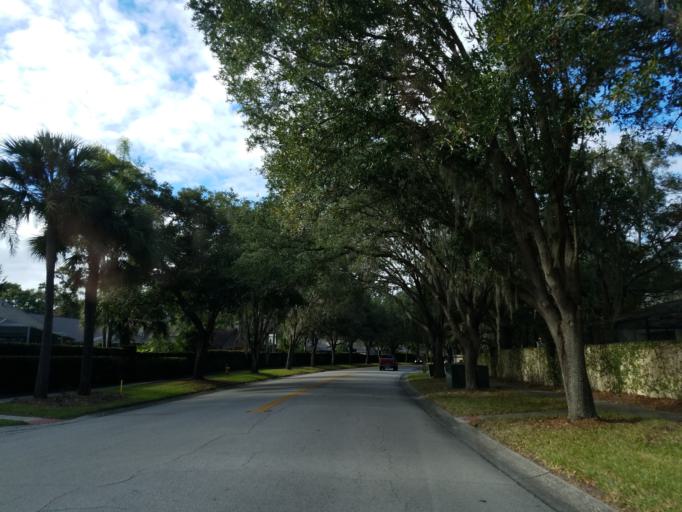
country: US
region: Florida
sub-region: Hillsborough County
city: Bloomingdale
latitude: 27.8846
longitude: -82.2462
